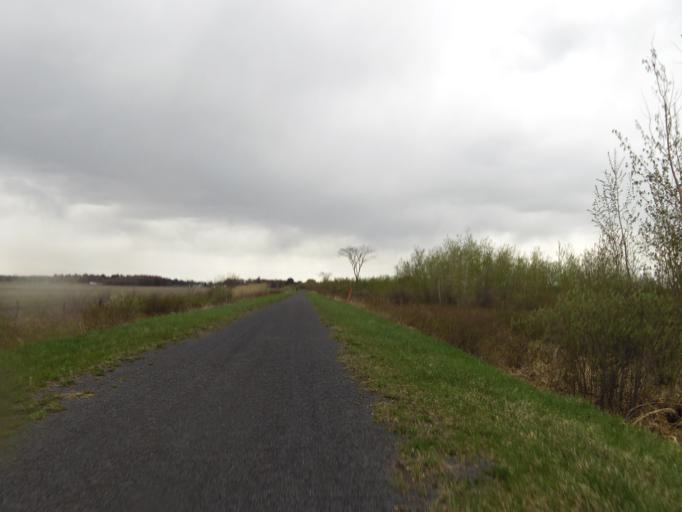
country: CA
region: Ontario
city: Bourget
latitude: 45.4454
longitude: -75.1308
